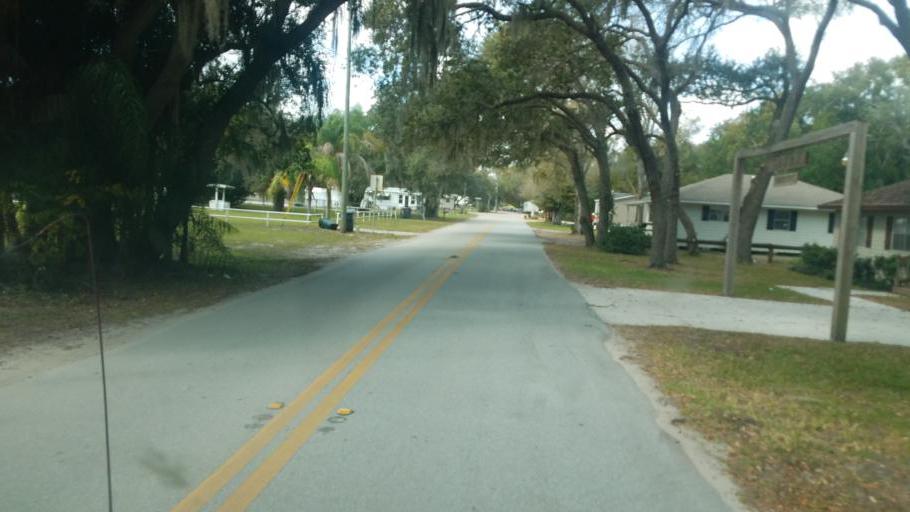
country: US
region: Florida
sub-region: Osceola County
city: Poinciana
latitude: 27.9765
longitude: -81.3754
